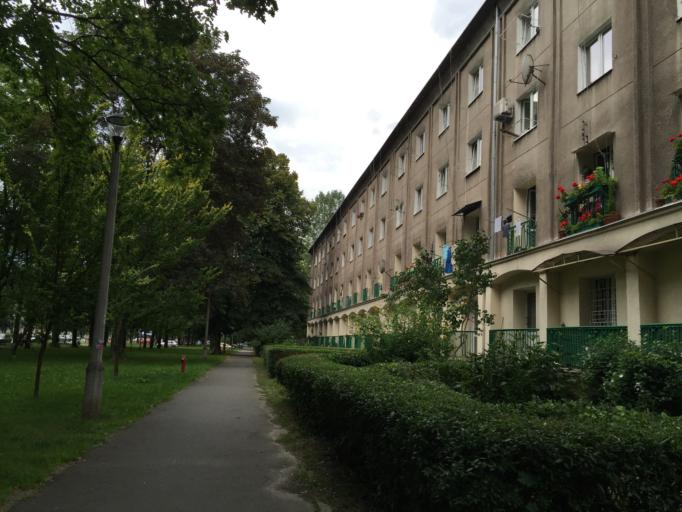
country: PL
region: Lesser Poland Voivodeship
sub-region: Powiat wielicki
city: Kokotow
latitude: 50.0790
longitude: 20.0345
